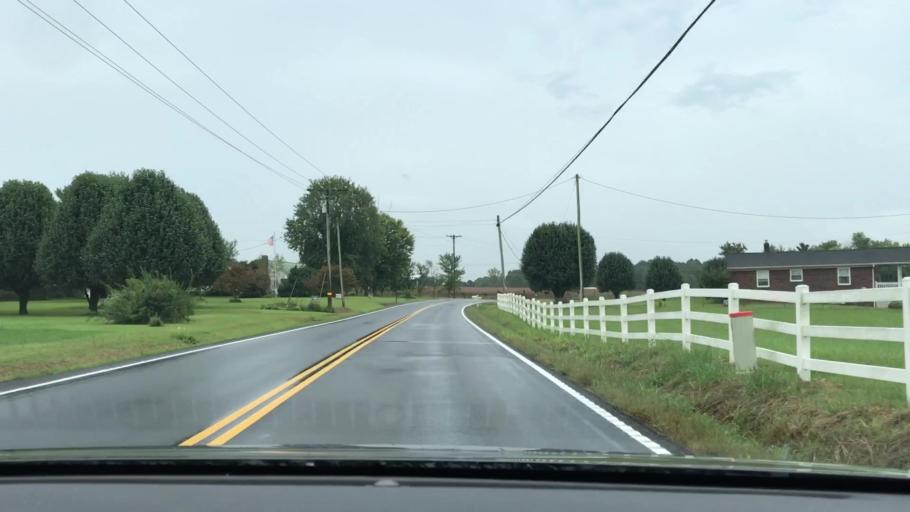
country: US
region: Tennessee
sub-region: Macon County
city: Red Boiling Springs
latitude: 36.4959
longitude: -85.8661
